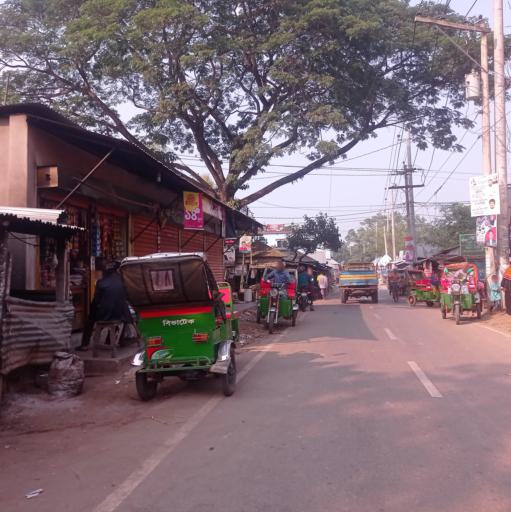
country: BD
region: Dhaka
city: Bhairab Bazar
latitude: 24.0807
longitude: 90.8490
